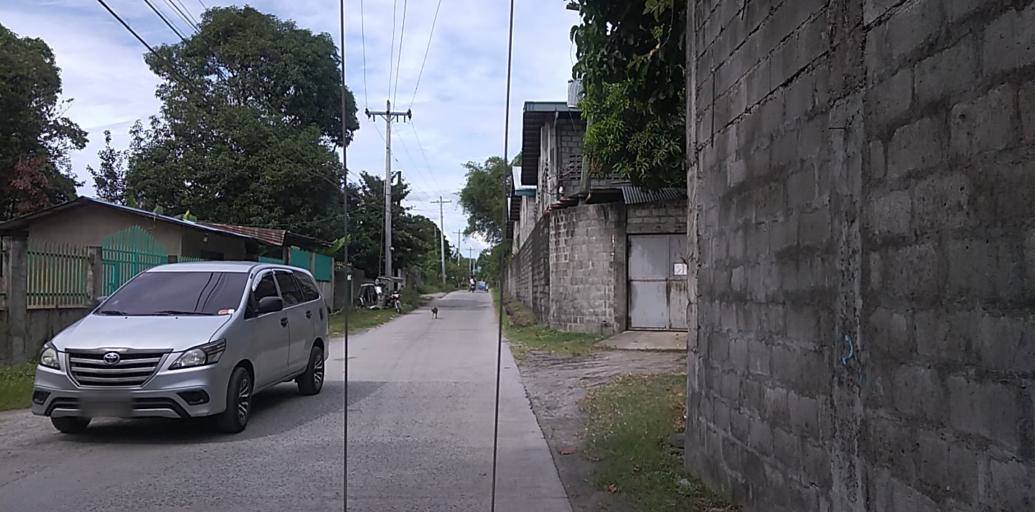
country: PH
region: Central Luzon
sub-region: Province of Pampanga
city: Manibaug Pasig
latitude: 15.1078
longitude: 120.5609
